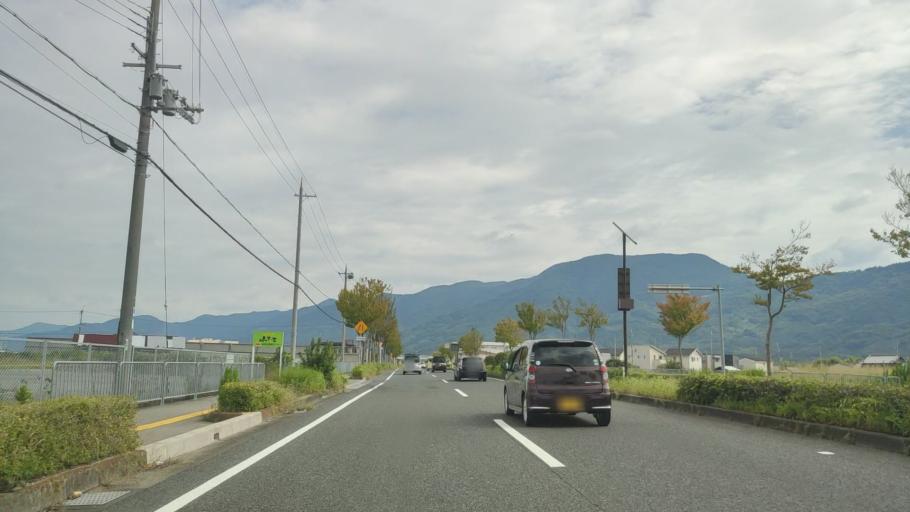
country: JP
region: Wakayama
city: Iwade
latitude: 34.2616
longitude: 135.3739
